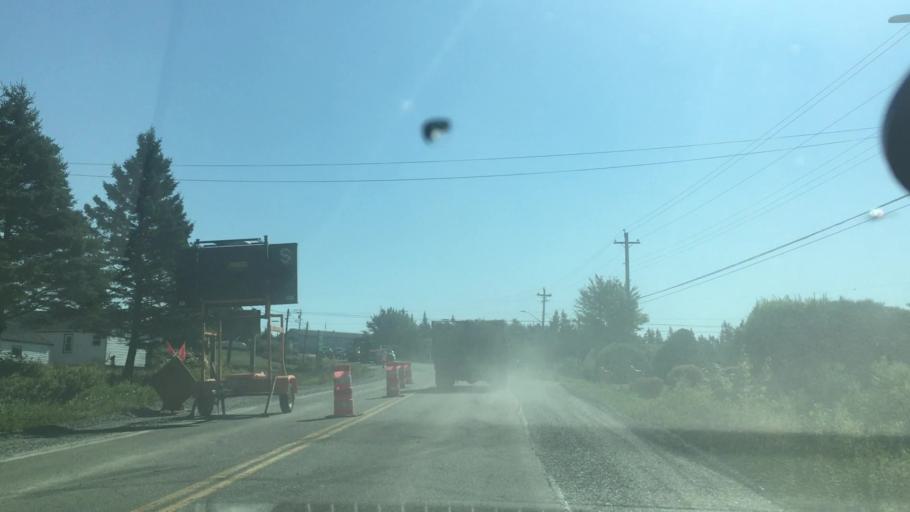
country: CA
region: Nova Scotia
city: New Glasgow
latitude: 44.9057
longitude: -62.4895
